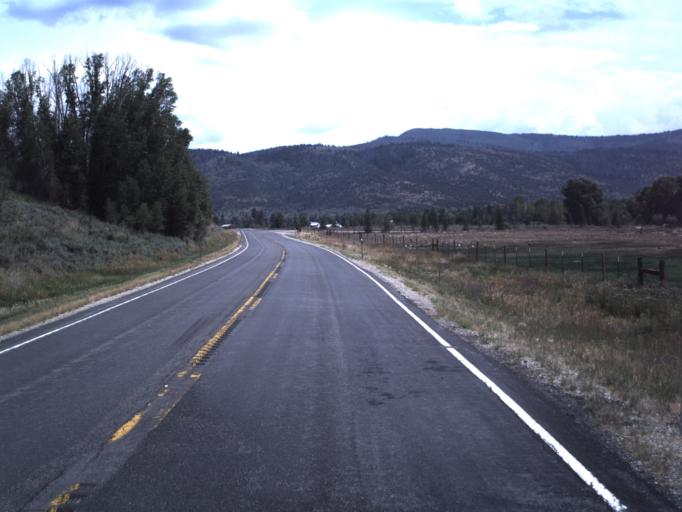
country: US
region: Utah
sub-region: Summit County
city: Francis
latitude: 40.5541
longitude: -111.1491
